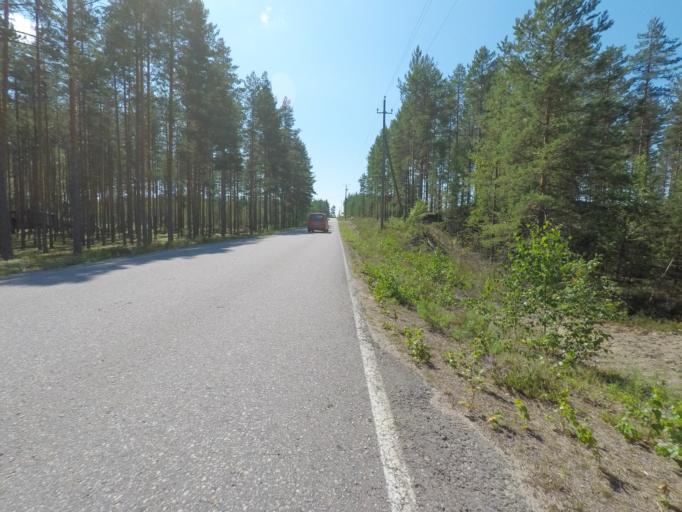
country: FI
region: Southern Savonia
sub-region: Mikkeli
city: Puumala
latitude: 61.4572
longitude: 28.1744
